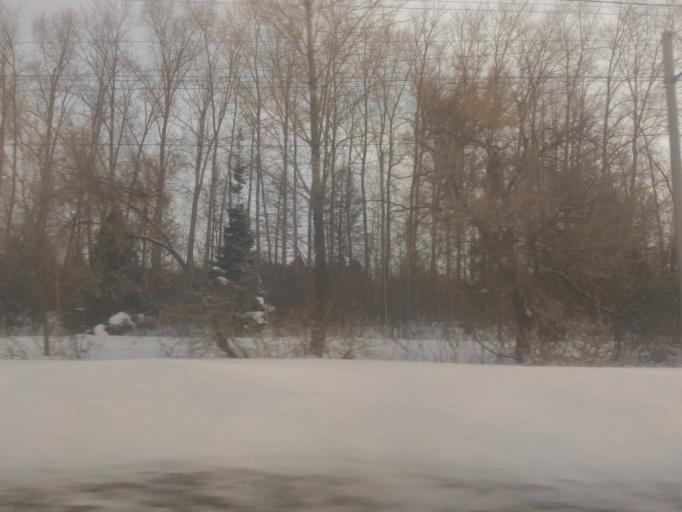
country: RU
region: Ulyanovsk
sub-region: Ulyanovskiy Rayon
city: Ulyanovsk
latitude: 54.3620
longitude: 48.3393
